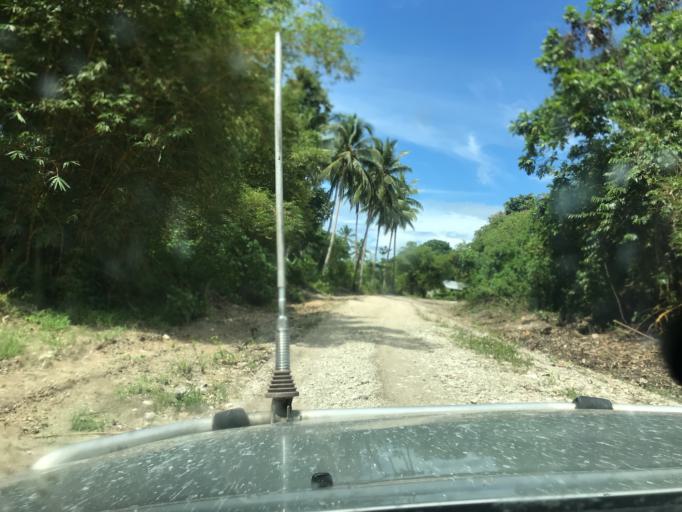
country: SB
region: Malaita
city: Auki
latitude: -8.4391
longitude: 160.8294
